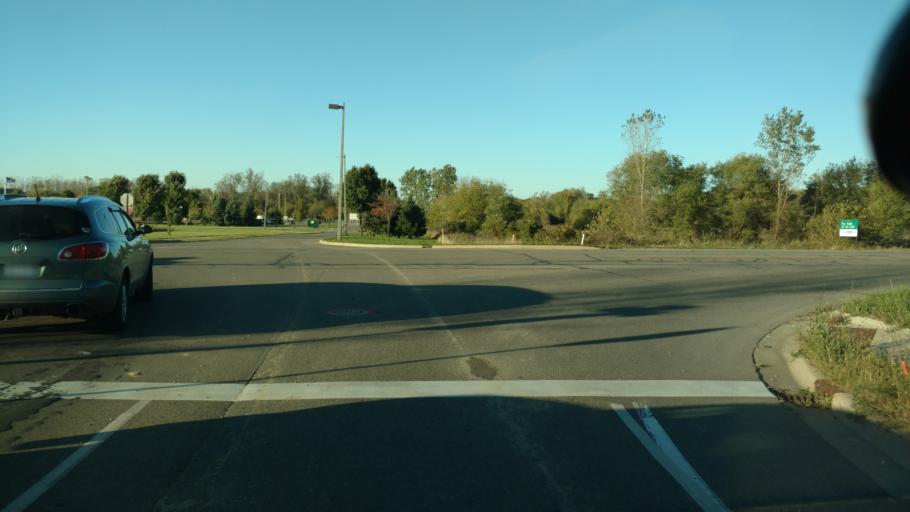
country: US
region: Michigan
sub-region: Ingham County
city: East Lansing
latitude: 42.7839
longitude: -84.5085
